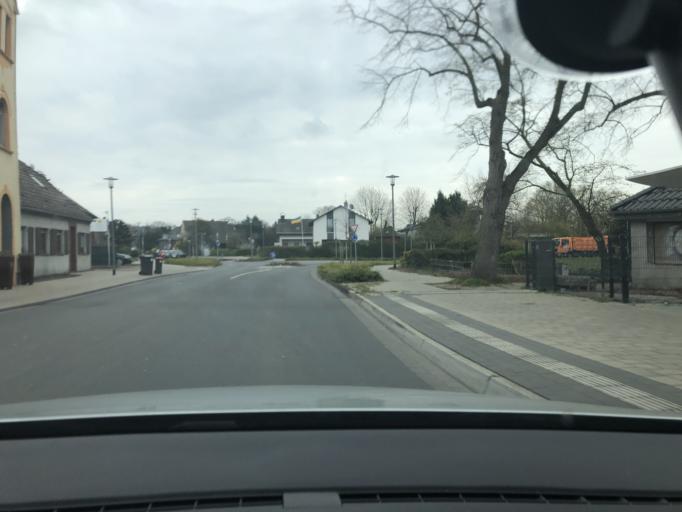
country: DE
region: North Rhine-Westphalia
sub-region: Regierungsbezirk Dusseldorf
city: Kamp-Lintfort
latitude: 51.4948
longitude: 6.5362
